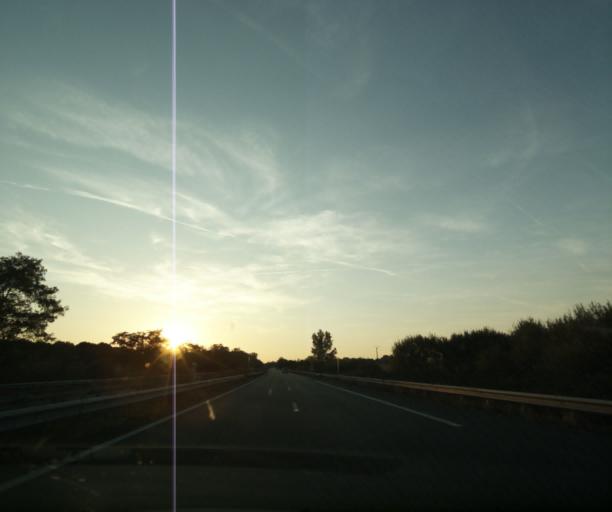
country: FR
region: Aquitaine
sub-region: Departement du Lot-et-Garonne
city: Tonneins
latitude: 44.3771
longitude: 0.2258
